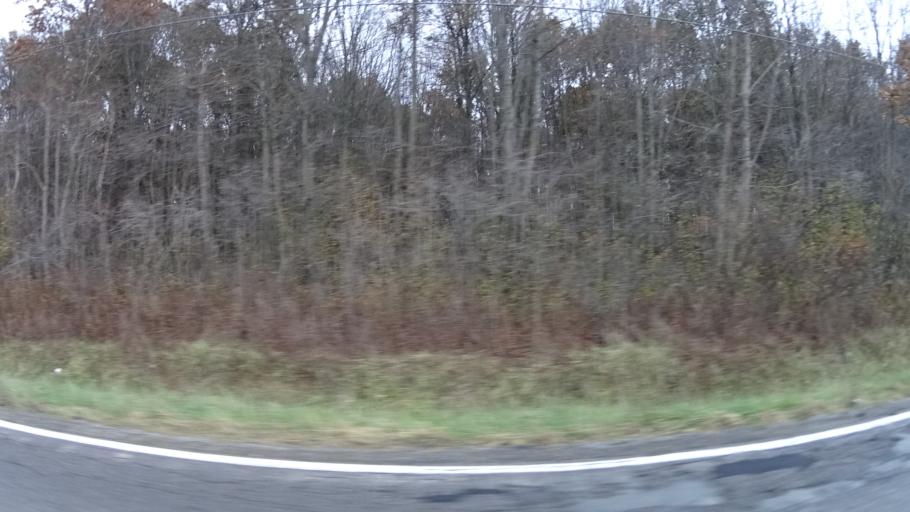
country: US
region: Ohio
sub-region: Lorain County
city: Elyria
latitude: 41.3512
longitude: -82.1261
